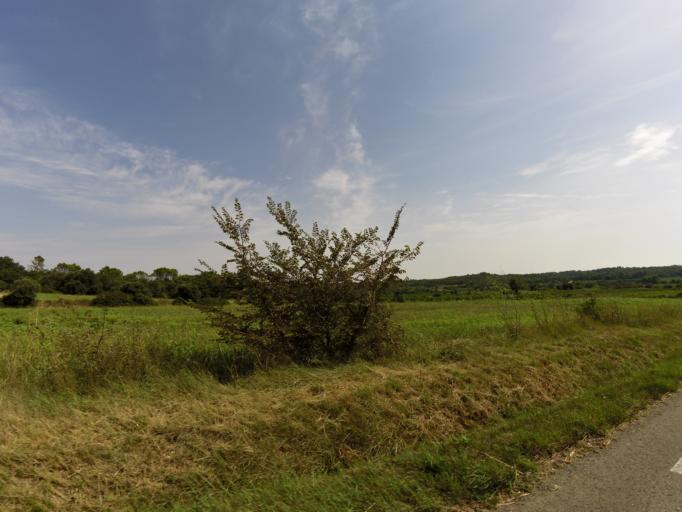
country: FR
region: Languedoc-Roussillon
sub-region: Departement du Gard
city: Villevieille
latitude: 43.8216
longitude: 4.0957
